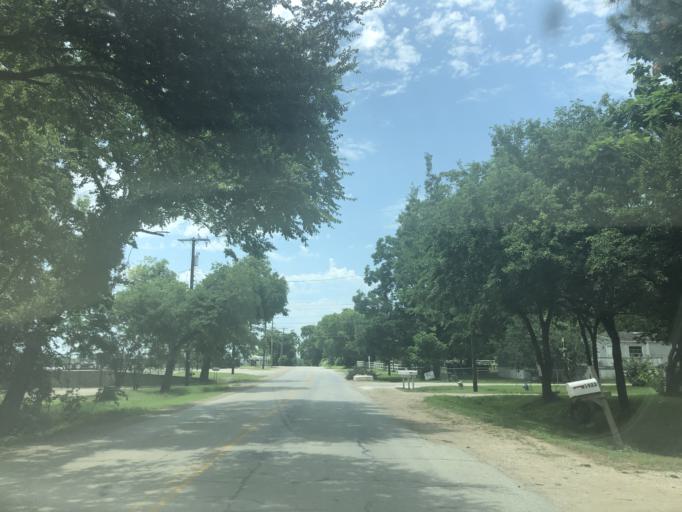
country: US
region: Texas
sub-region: Dallas County
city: Irving
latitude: 32.7905
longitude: -96.9345
